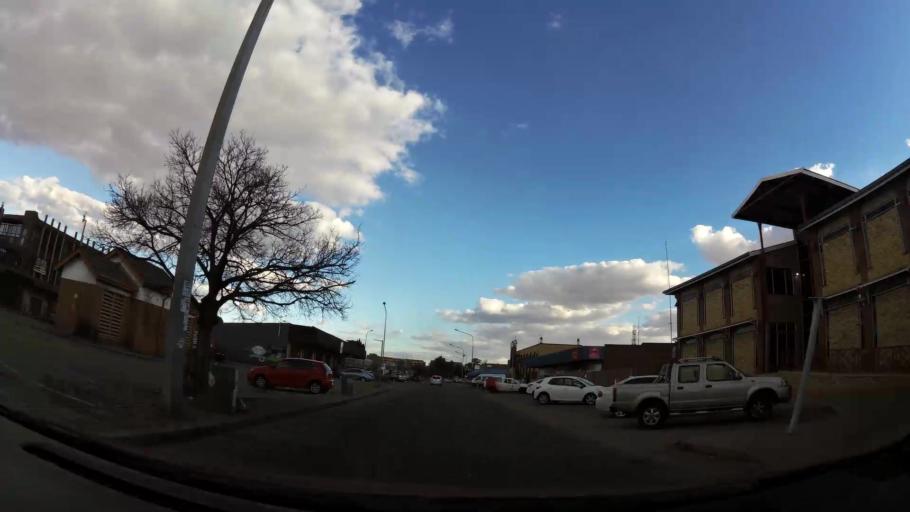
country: ZA
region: North-West
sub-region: Dr Kenneth Kaunda District Municipality
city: Potchefstroom
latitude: -26.7127
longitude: 27.0962
